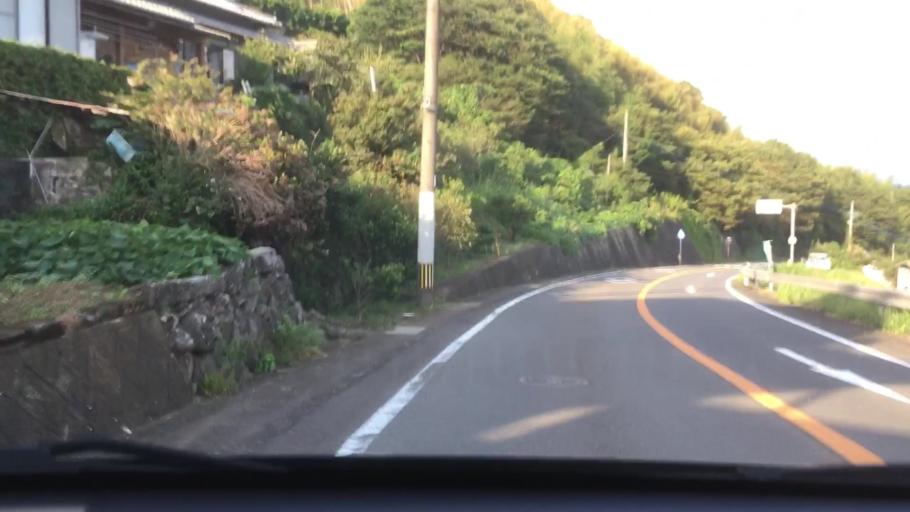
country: JP
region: Nagasaki
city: Sasebo
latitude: 33.0479
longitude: 129.7241
